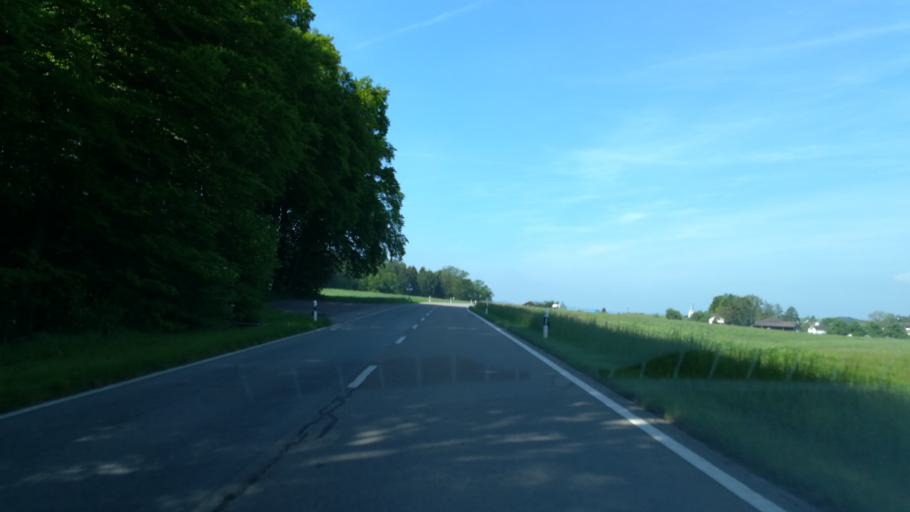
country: CH
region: Thurgau
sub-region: Weinfelden District
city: Wigoltingen
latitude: 47.6081
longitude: 9.0227
